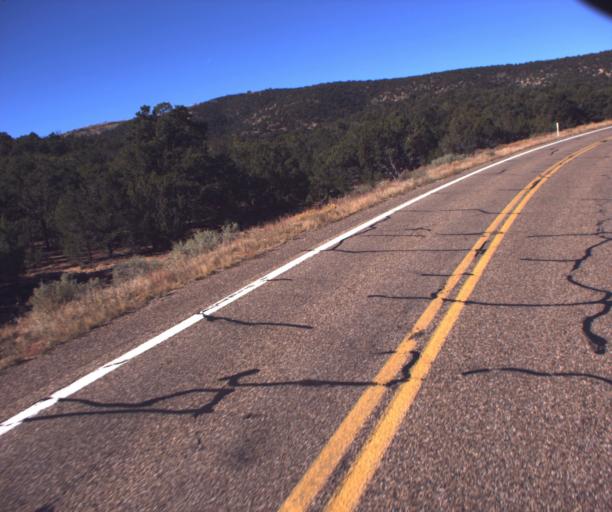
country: US
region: Arizona
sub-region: Coconino County
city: Fredonia
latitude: 36.7394
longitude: -112.1059
